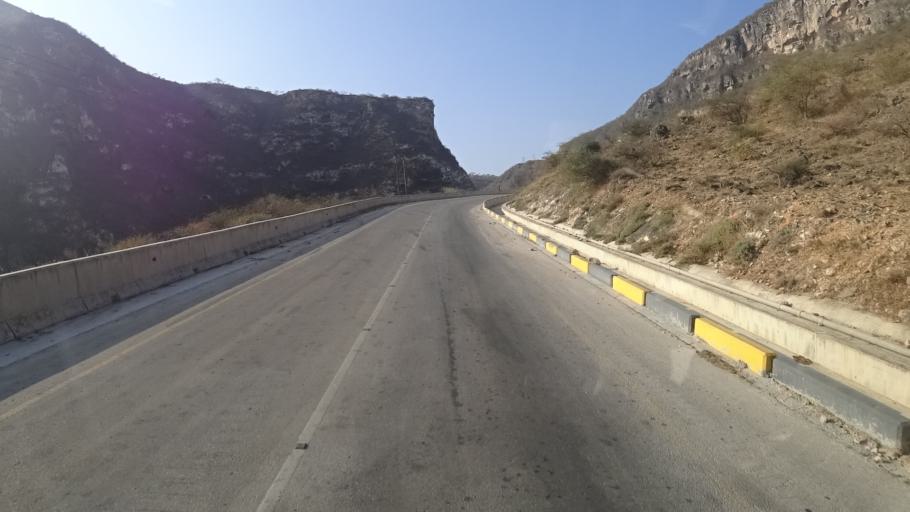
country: YE
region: Al Mahrah
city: Hawf
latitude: 16.7417
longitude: 53.2291
